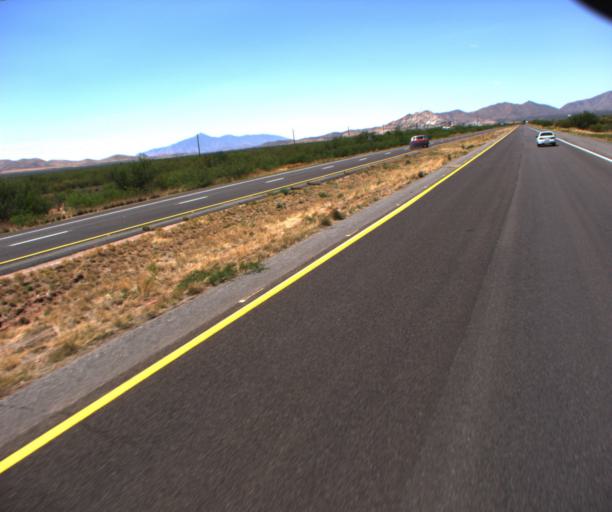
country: US
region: Arizona
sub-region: Cochise County
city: Pirtleville
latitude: 31.3646
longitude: -109.7000
